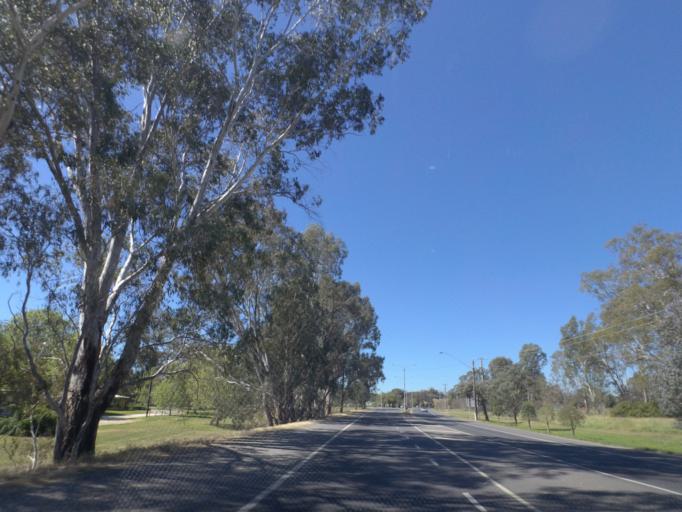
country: AU
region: Victoria
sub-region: Murrindindi
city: Kinglake West
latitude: -37.0232
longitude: 145.1144
